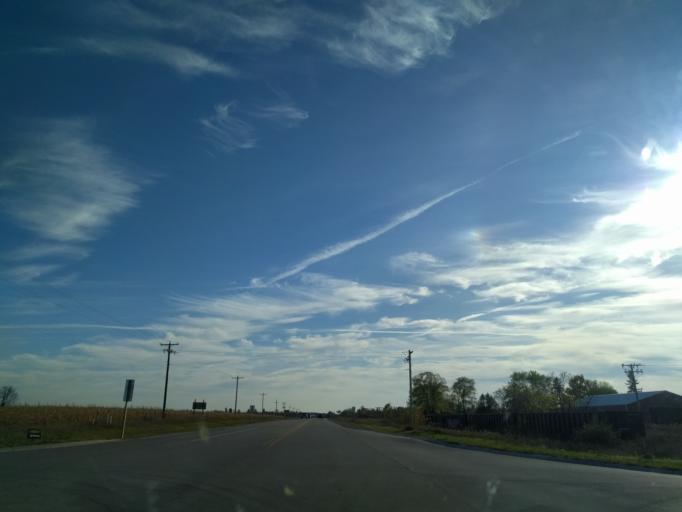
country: US
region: Wisconsin
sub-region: Marinette County
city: Peshtigo
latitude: 45.3670
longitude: -87.9529
